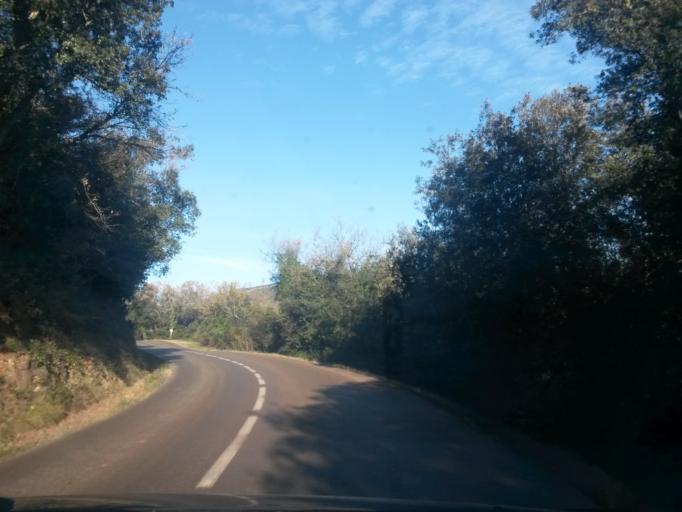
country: ES
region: Catalonia
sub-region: Provincia de Girona
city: Sant Gregori
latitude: 42.0142
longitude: 2.6739
